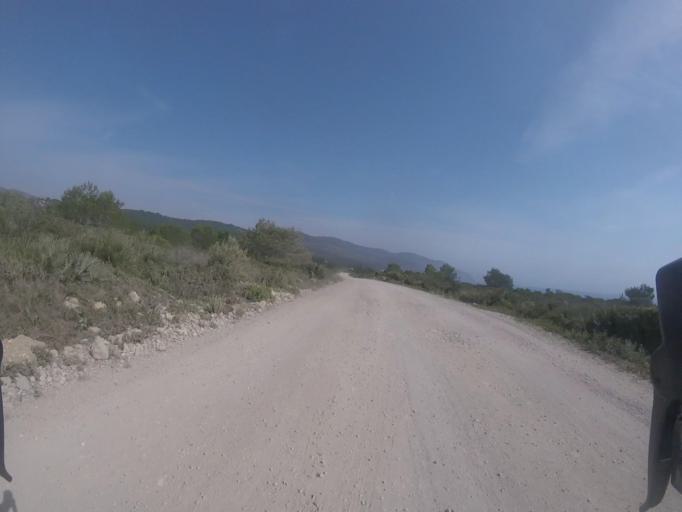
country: ES
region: Valencia
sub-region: Provincia de Castello
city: Santa Magdalena de Pulpis
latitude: 40.3035
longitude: 0.3503
